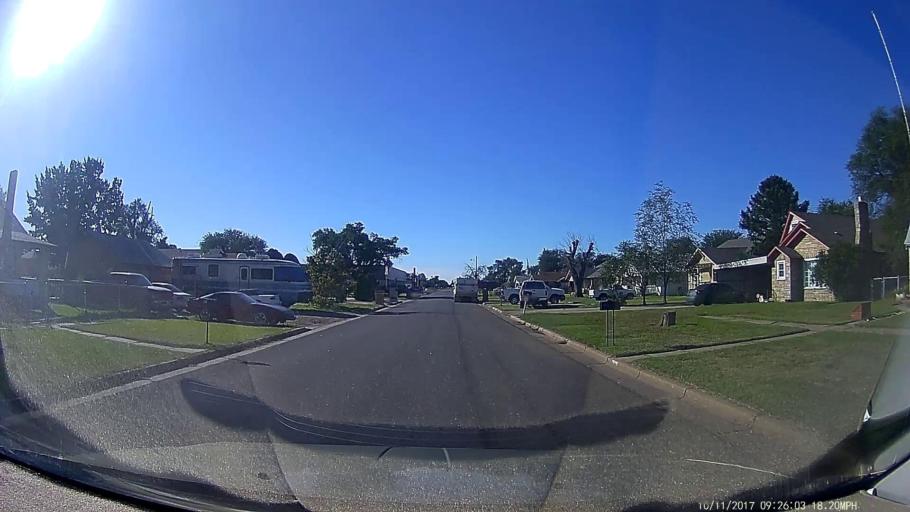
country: US
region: New Mexico
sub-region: Curry County
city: Clovis
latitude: 34.4067
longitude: -103.2103
